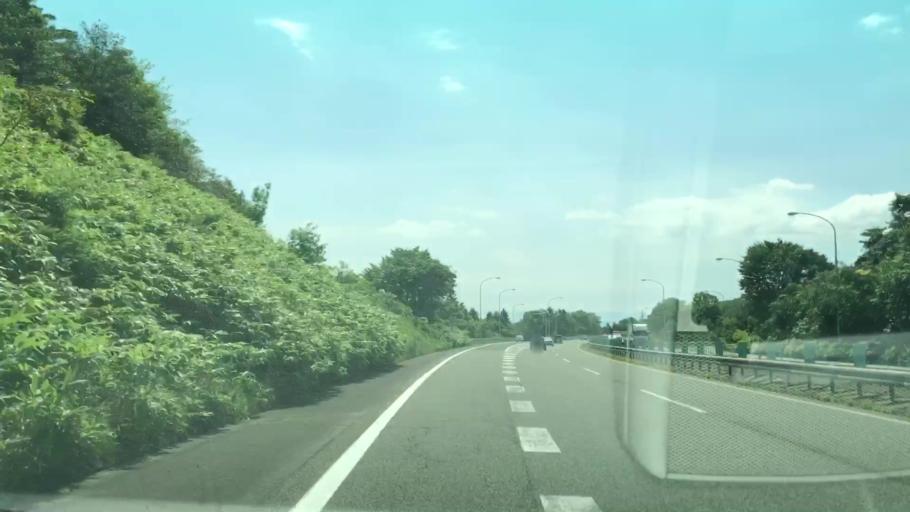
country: JP
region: Hokkaido
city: Muroran
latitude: 42.4026
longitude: 141.0816
